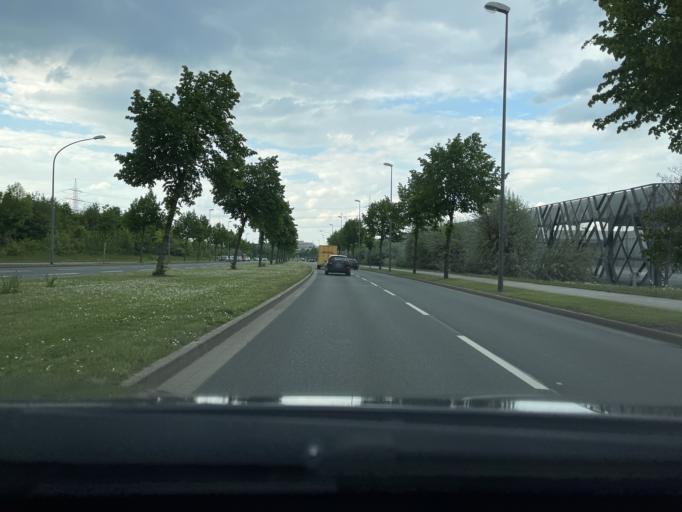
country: DE
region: North Rhine-Westphalia
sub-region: Regierungsbezirk Dusseldorf
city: Essen
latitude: 51.4610
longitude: 6.9888
